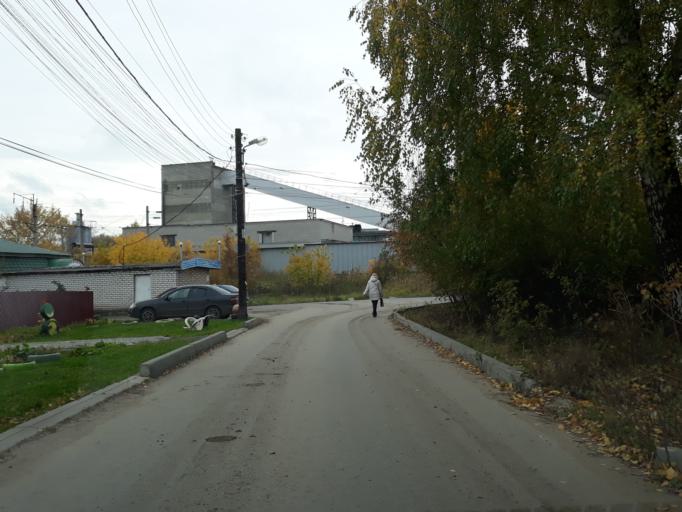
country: RU
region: Nizjnij Novgorod
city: Nizhniy Novgorod
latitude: 56.2512
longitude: 43.9858
